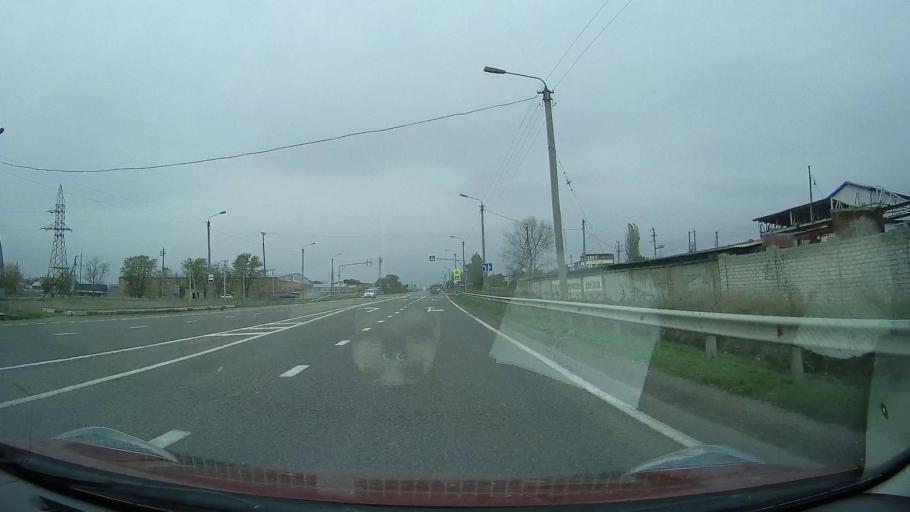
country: RU
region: Stavropol'skiy
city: Levokumka
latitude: 44.2519
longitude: 43.1266
